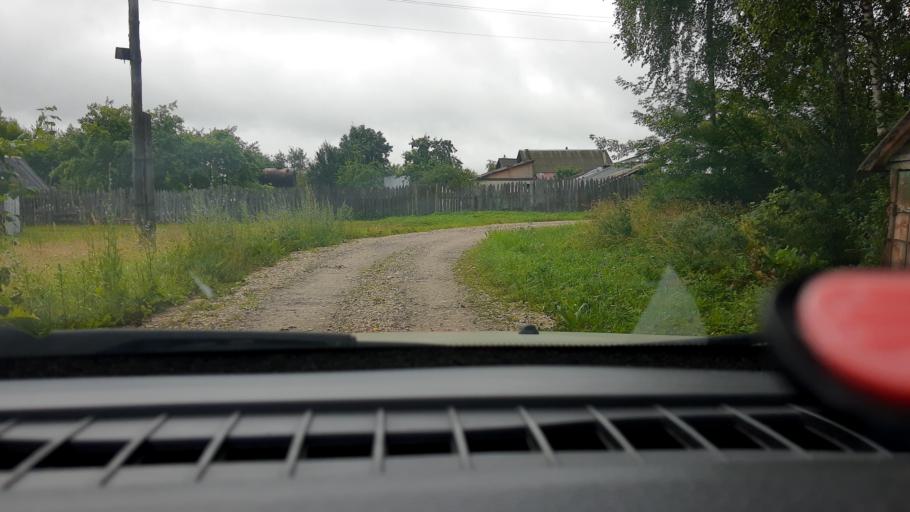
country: RU
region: Vladimir
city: Luknovo
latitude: 56.2248
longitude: 42.0216
